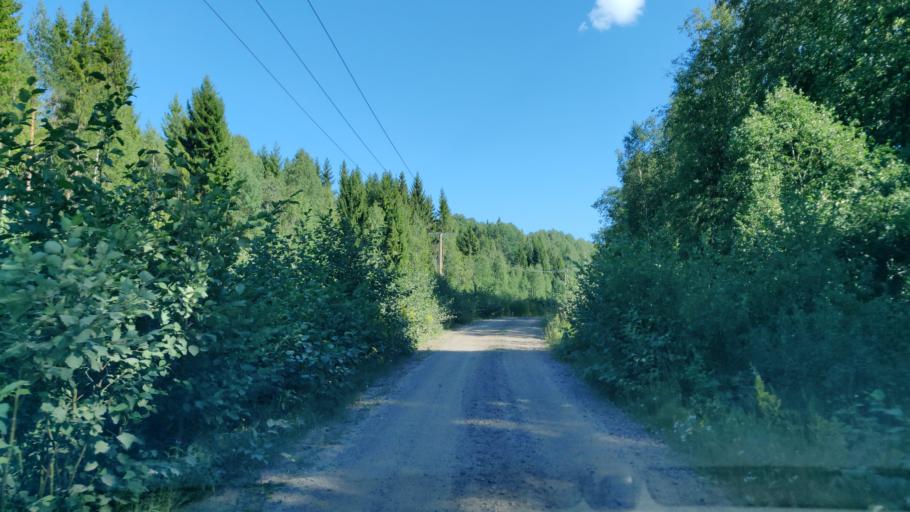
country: SE
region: Vaermland
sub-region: Hagfors Kommun
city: Ekshaerad
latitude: 60.0485
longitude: 13.5241
